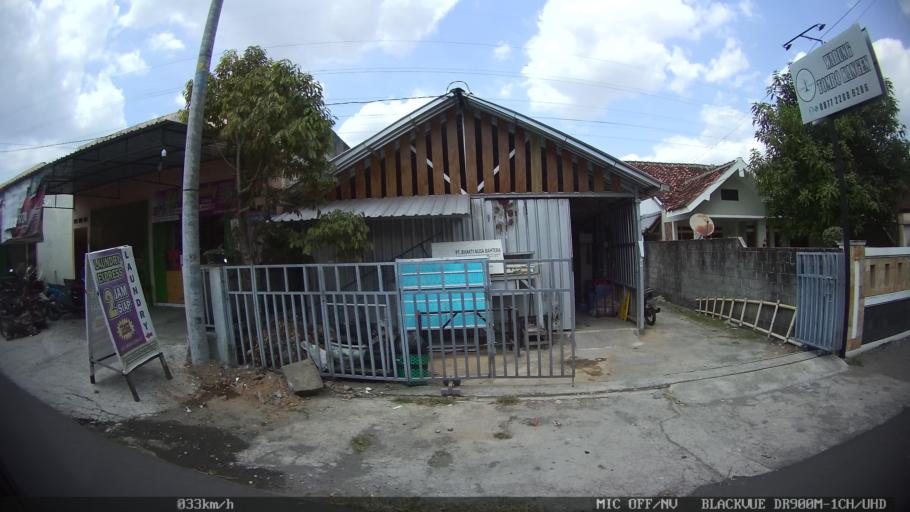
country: ID
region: Daerah Istimewa Yogyakarta
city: Gamping Lor
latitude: -7.8090
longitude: 110.3405
